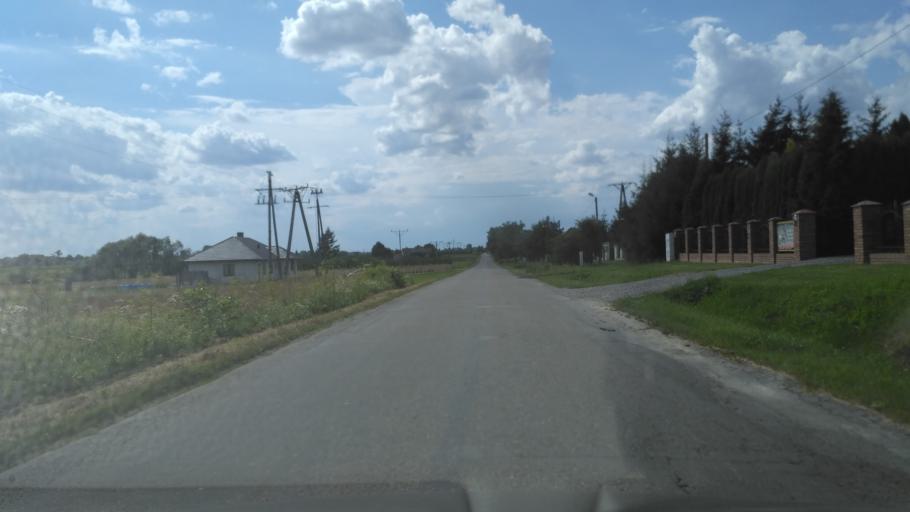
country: PL
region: Lublin Voivodeship
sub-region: Powiat leczynski
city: Milejow
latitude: 51.2140
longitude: 22.9254
